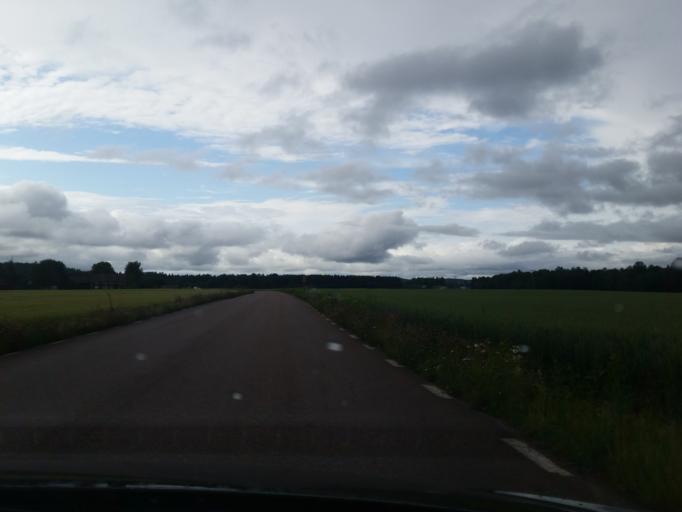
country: SE
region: Dalarna
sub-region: Leksand Municipality
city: Smedby
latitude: 60.7089
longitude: 15.0337
